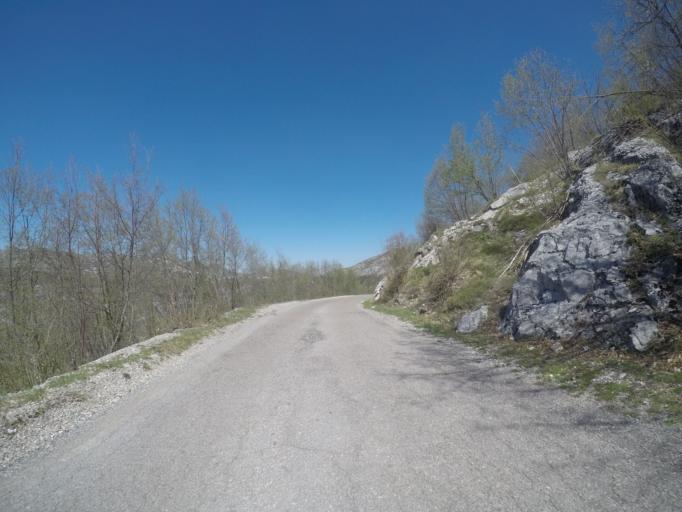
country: ME
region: Cetinje
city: Cetinje
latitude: 42.4510
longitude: 18.8738
